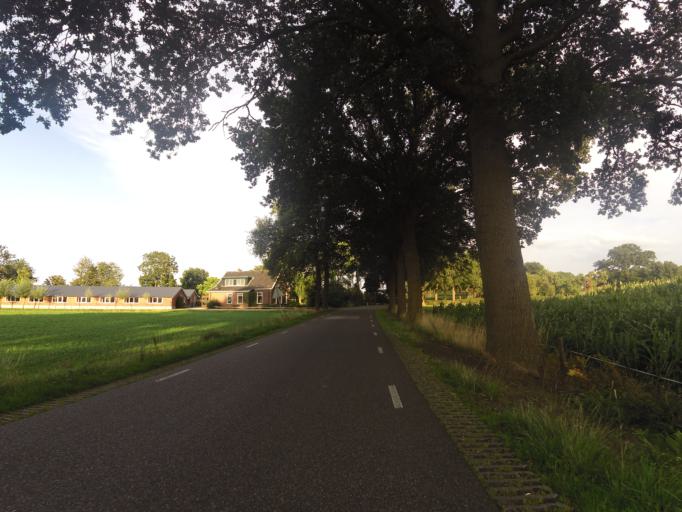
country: NL
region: Gelderland
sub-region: Oude IJsselstreek
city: Varsseveld
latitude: 51.9151
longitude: 6.4847
